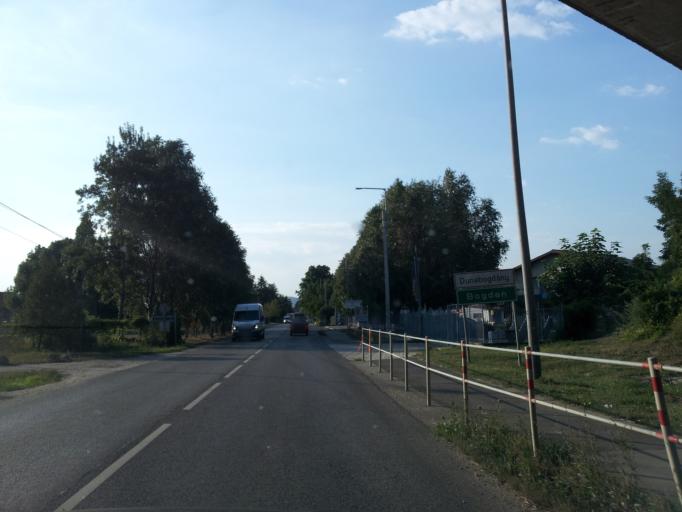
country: HU
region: Pest
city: Dunabogdany
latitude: 47.7887
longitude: 19.0422
